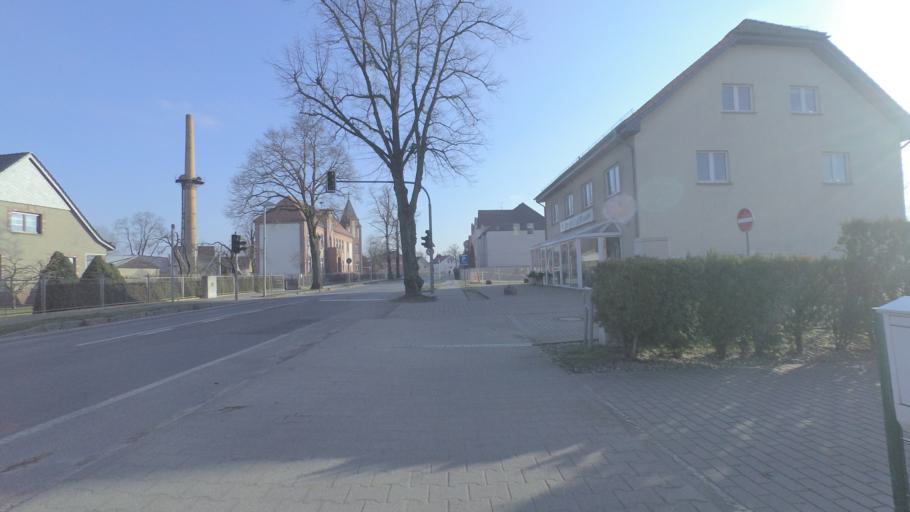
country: DE
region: Brandenburg
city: Zossen
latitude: 52.2411
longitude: 13.4310
